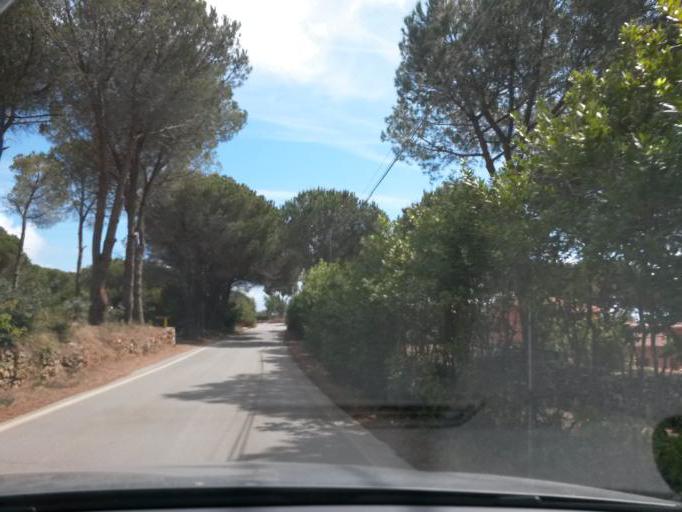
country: IT
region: Tuscany
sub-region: Provincia di Livorno
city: Porto Azzurro
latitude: 42.7542
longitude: 10.3927
